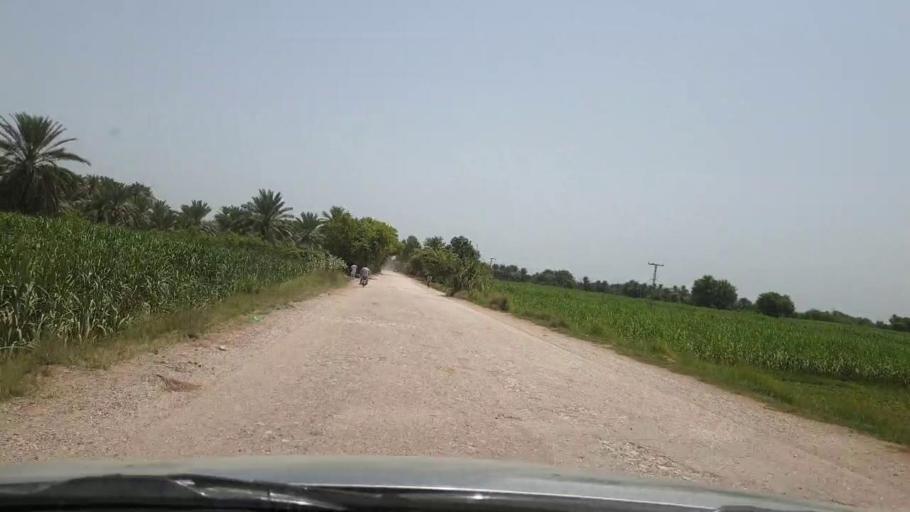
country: PK
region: Sindh
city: Pano Aqil
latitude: 27.8600
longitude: 69.0890
